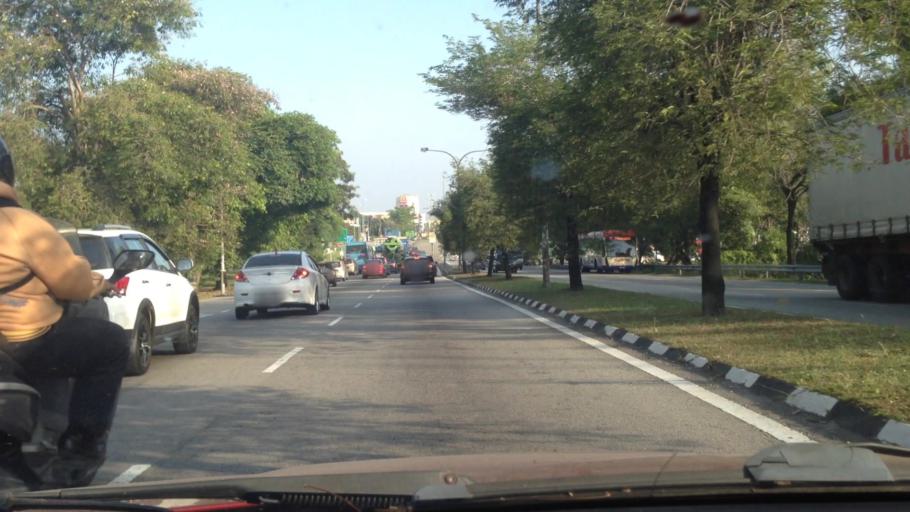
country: MY
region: Selangor
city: Subang Jaya
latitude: 3.0452
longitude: 101.5458
